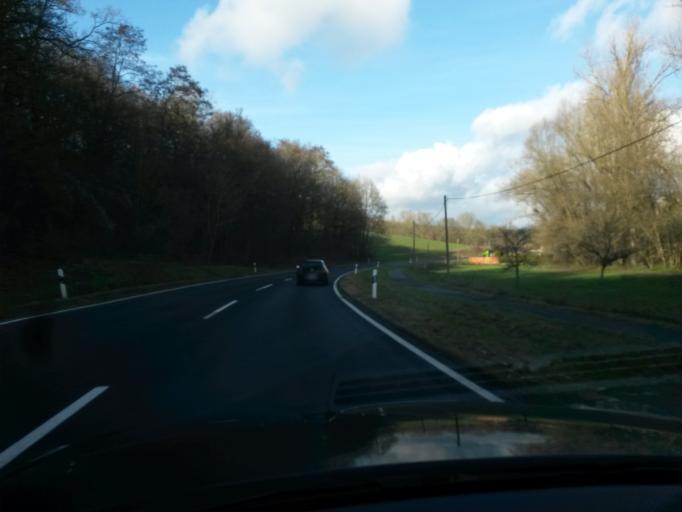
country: DE
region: Bavaria
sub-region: Regierungsbezirk Unterfranken
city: Rimpar
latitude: 49.8272
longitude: 9.9564
